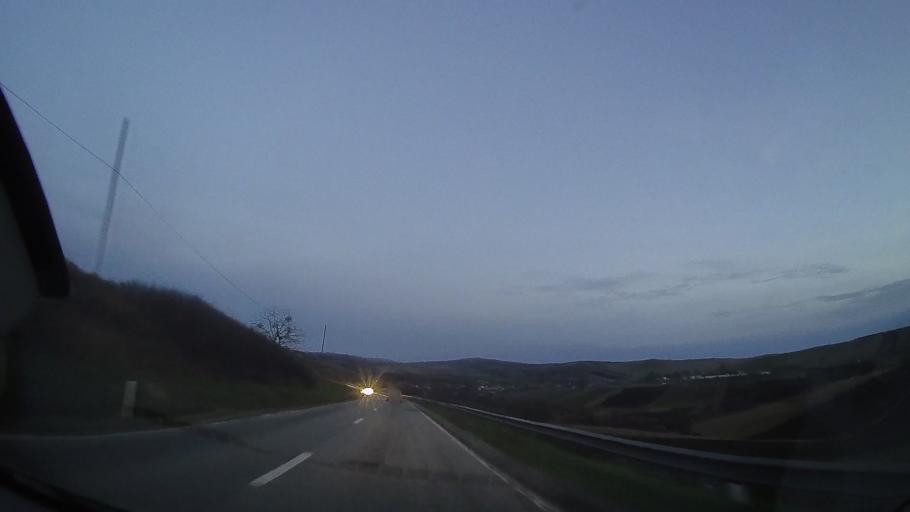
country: RO
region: Cluj
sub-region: Comuna Camarasu
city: Camarasu
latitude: 46.7936
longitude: 24.1127
